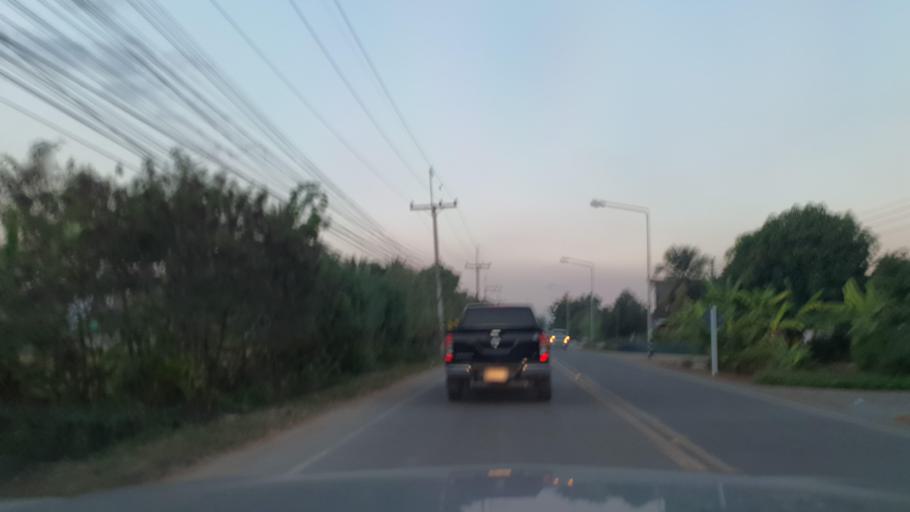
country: TH
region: Phayao
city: Dok Kham Tai
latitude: 19.0837
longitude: 100.0630
